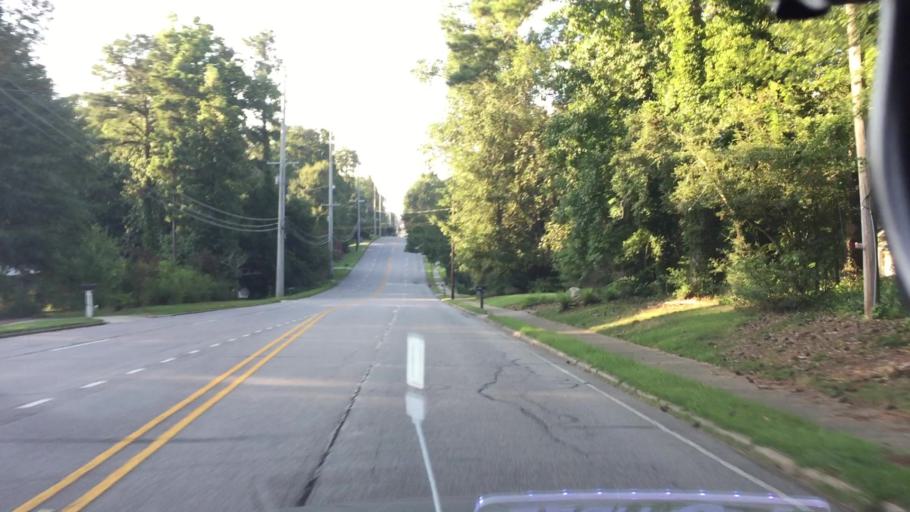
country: US
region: Alabama
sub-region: Lee County
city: Auburn
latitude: 32.5928
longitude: -85.4647
